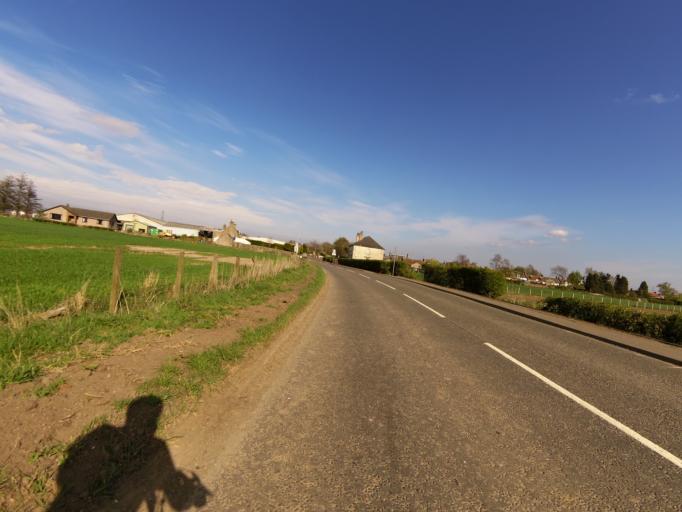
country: GB
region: Scotland
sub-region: Fife
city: Auchtermuchty
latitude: 56.2818
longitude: -3.2179
